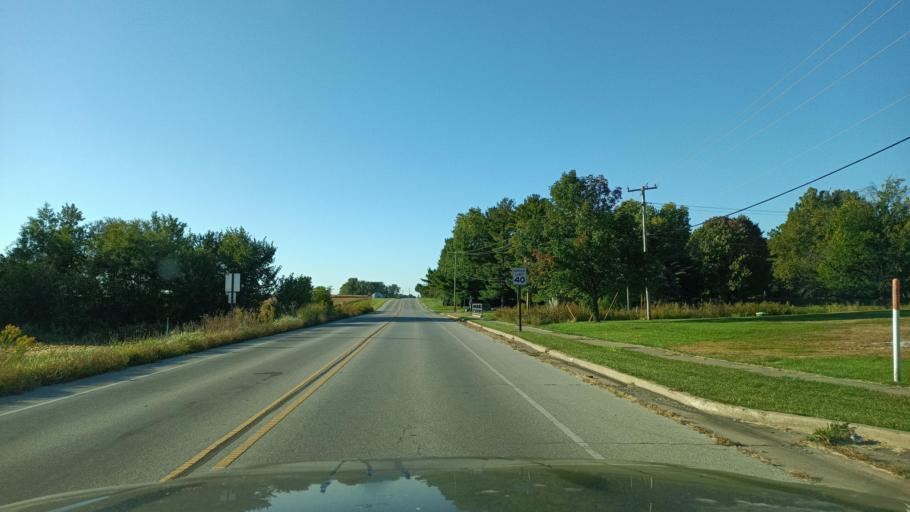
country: US
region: Illinois
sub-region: Champaign County
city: Savoy
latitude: 40.0660
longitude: -88.2384
